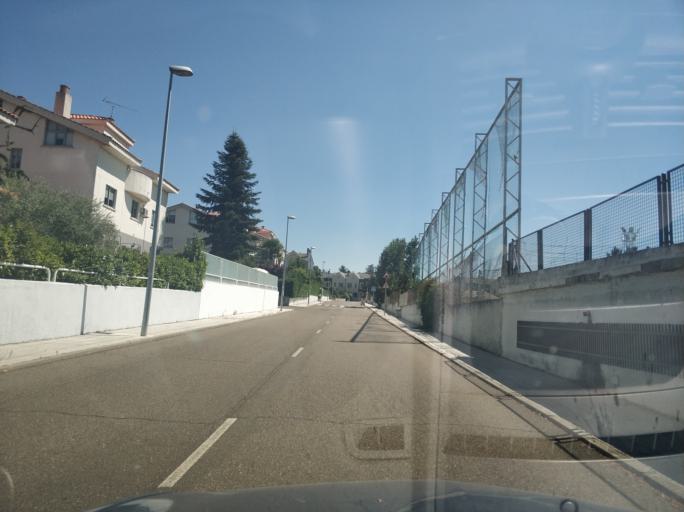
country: ES
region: Castille and Leon
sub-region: Provincia de Salamanca
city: Villares de la Reina
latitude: 40.9962
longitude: -5.6611
